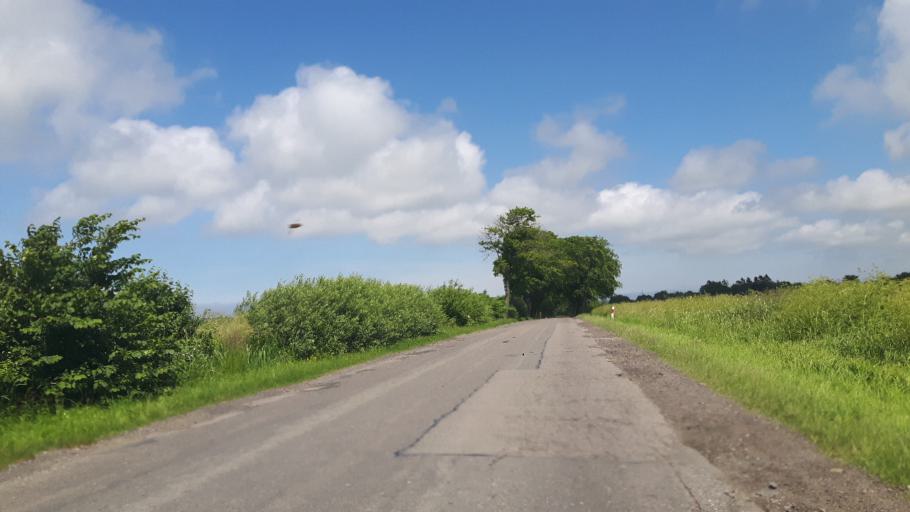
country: PL
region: Pomeranian Voivodeship
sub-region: Powiat slupski
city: Ustka
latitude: 54.5469
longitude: 16.8279
